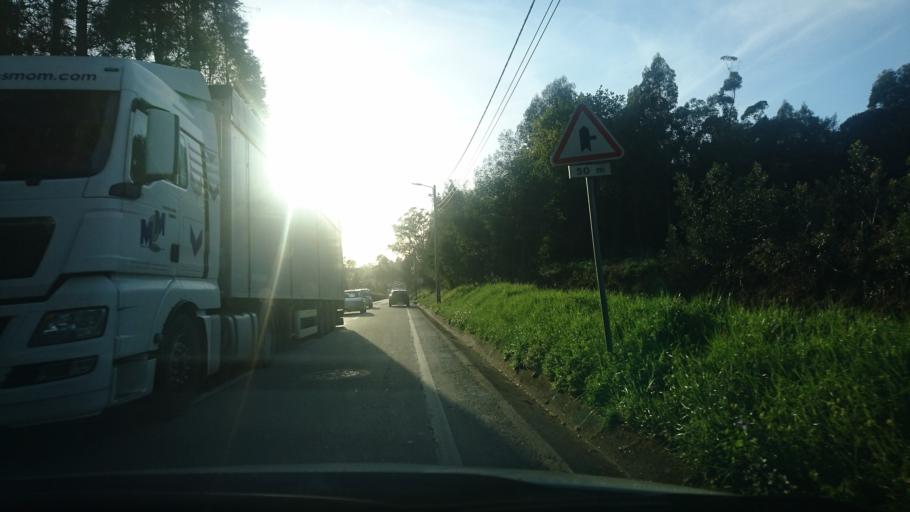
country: PT
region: Aveiro
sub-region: Santa Maria da Feira
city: Pacos de Brandao
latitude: 40.9828
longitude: -8.5947
